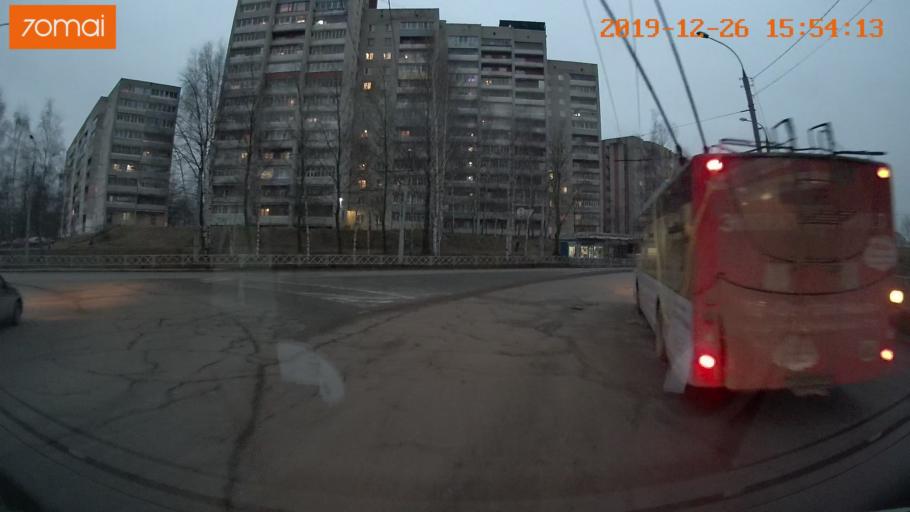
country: RU
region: Jaroslavl
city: Rybinsk
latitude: 58.0457
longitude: 38.8208
